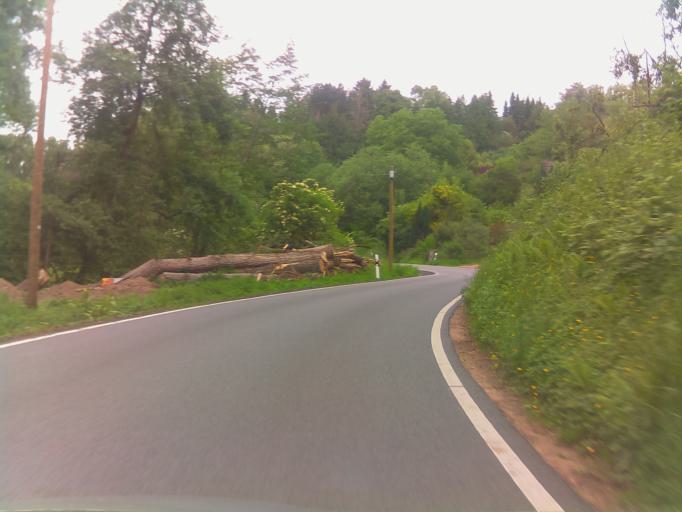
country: DE
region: Bavaria
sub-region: Regierungsbezirk Unterfranken
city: Glattbach
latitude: 49.9984
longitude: 9.1250
